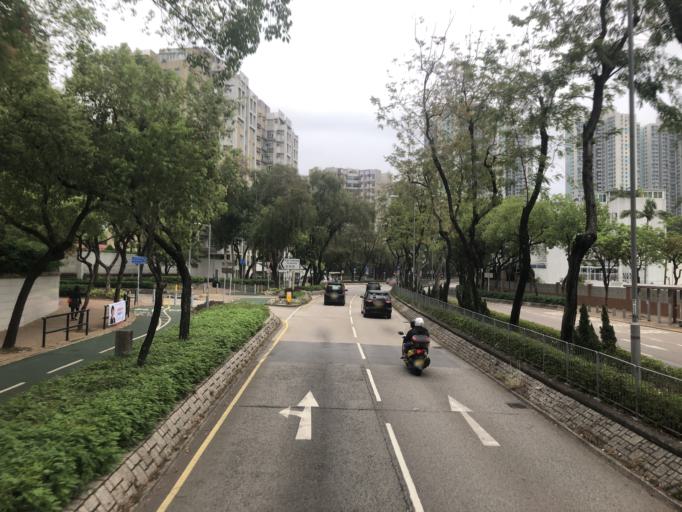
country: HK
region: Tai Po
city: Tai Po
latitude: 22.4956
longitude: 114.1306
